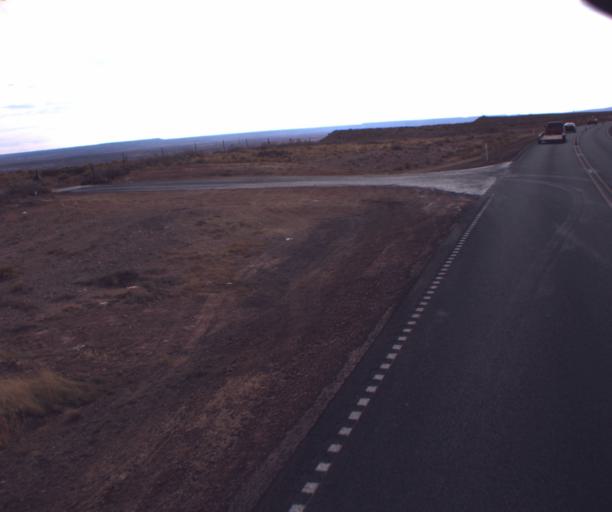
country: US
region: Arizona
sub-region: Apache County
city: Chinle
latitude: 36.0704
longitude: -109.6104
